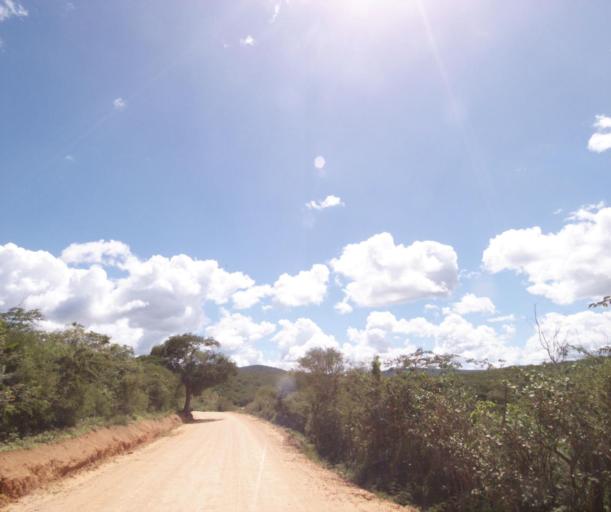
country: BR
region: Bahia
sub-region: Pocoes
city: Pocoes
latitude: -14.2980
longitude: -40.6400
